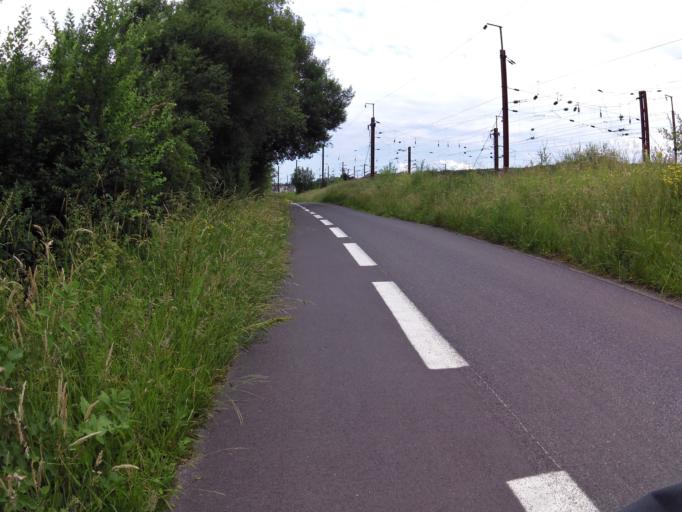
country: FR
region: Champagne-Ardenne
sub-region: Departement des Ardennes
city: Lumes
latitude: 49.7254
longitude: 4.7843
